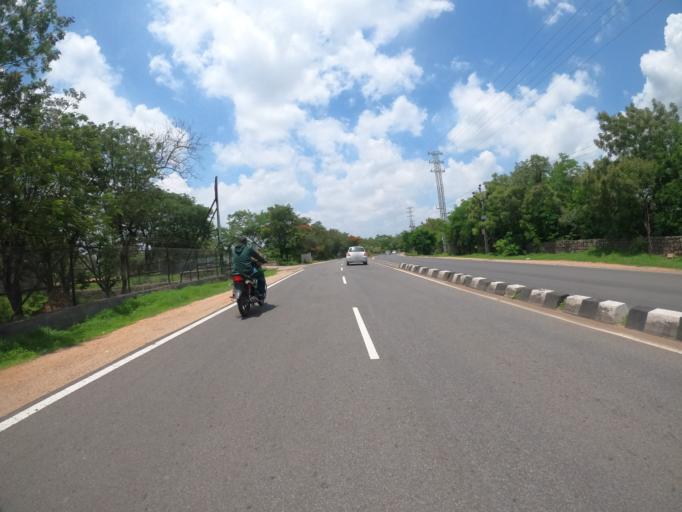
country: IN
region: Telangana
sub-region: Hyderabad
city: Hyderabad
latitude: 17.3521
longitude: 78.3548
